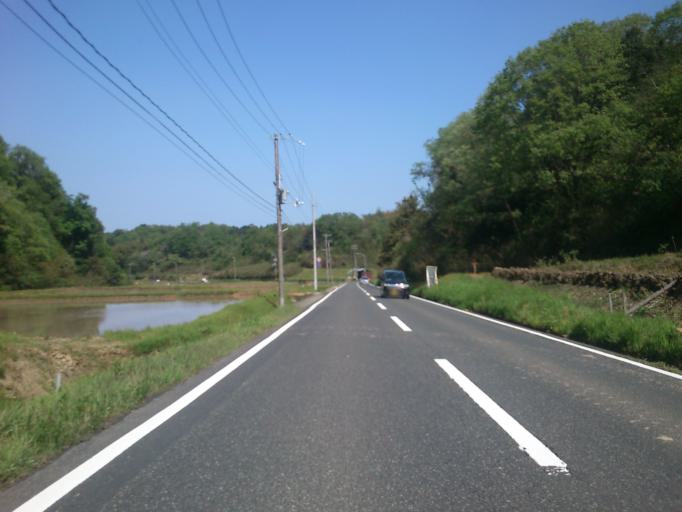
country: JP
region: Kyoto
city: Miyazu
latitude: 35.6819
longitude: 135.0674
